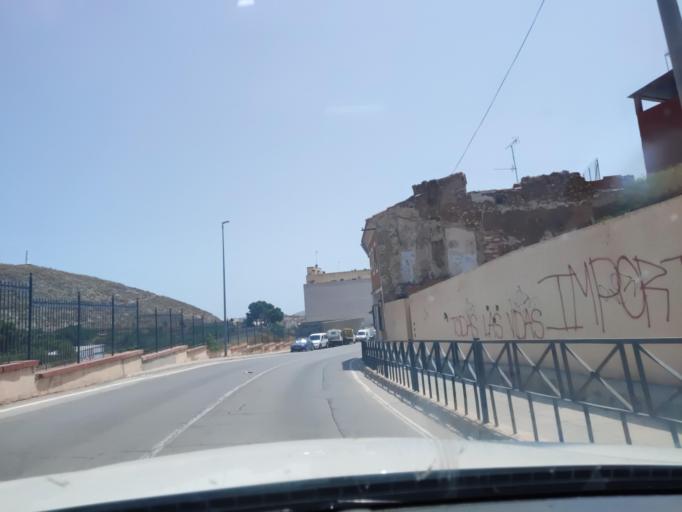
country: ES
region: Castille-La Mancha
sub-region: Provincia de Albacete
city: Hellin
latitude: 38.5153
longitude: -1.6973
